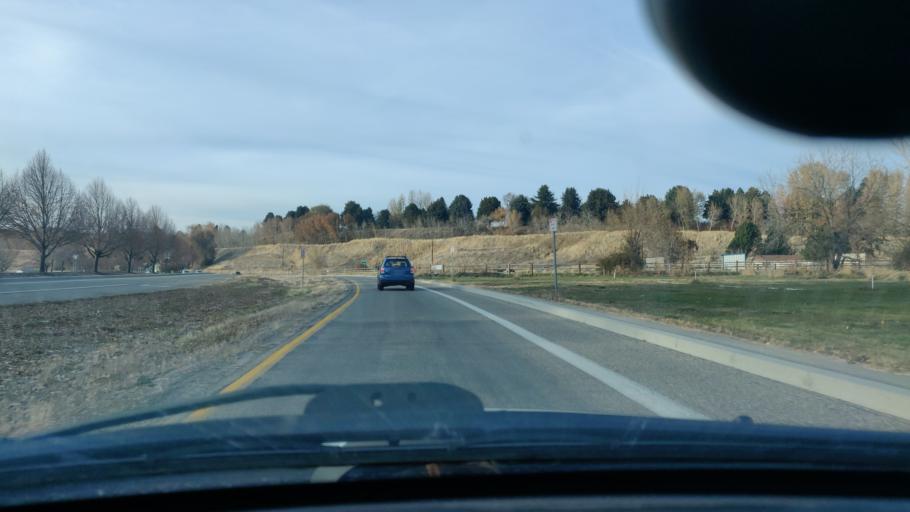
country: US
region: Idaho
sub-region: Ada County
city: Eagle
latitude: 43.6886
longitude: -116.3026
